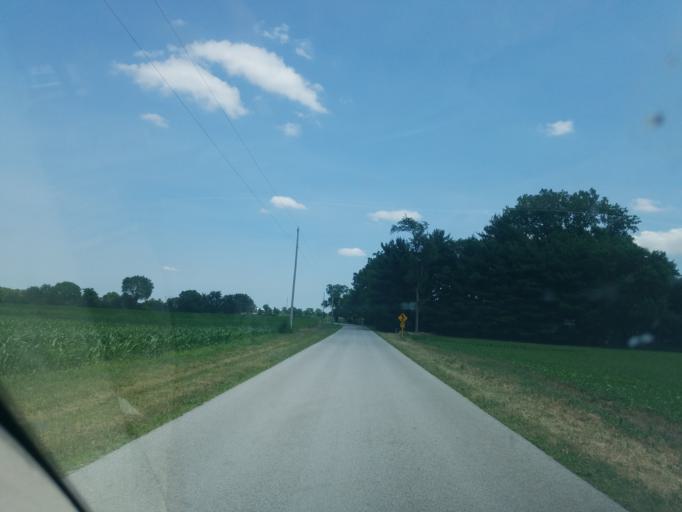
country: US
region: Ohio
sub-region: Wyandot County
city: Carey
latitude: 40.9465
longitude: -83.5102
